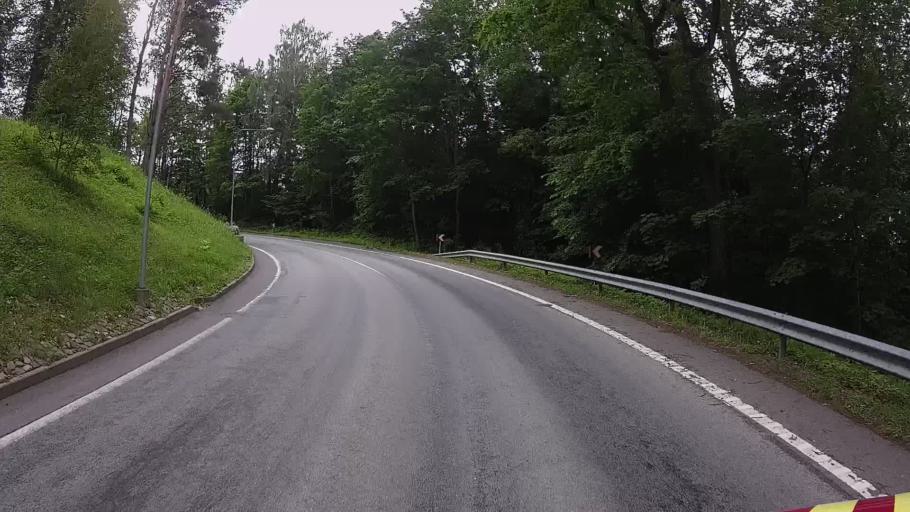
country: EE
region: Viljandimaa
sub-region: Karksi vald
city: Karksi-Nuia
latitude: 58.1084
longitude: 25.5461
